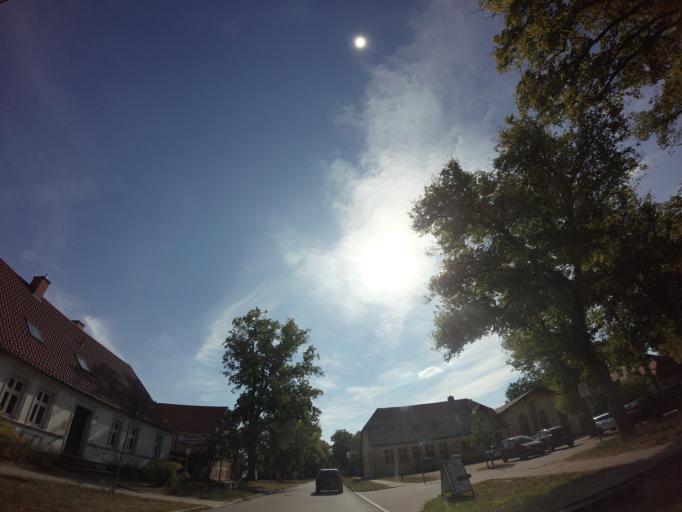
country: DE
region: Brandenburg
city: Grosswoltersdorf
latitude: 53.1033
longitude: 13.0512
